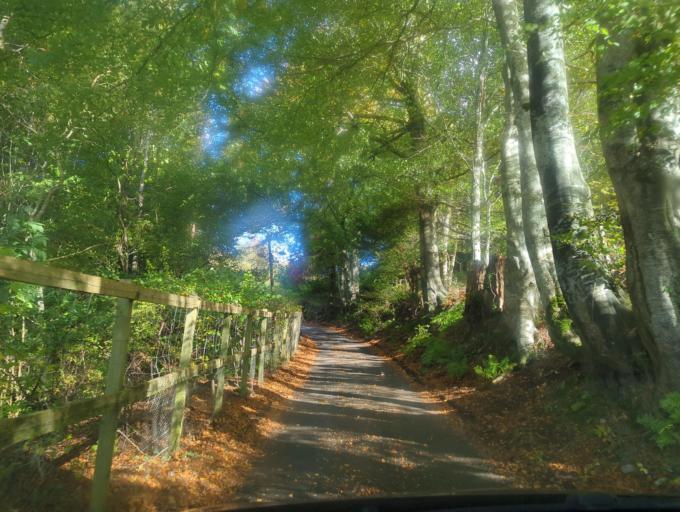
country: GB
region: Scotland
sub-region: Perth and Kinross
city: Bankfoot
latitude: 56.5686
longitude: -3.5848
